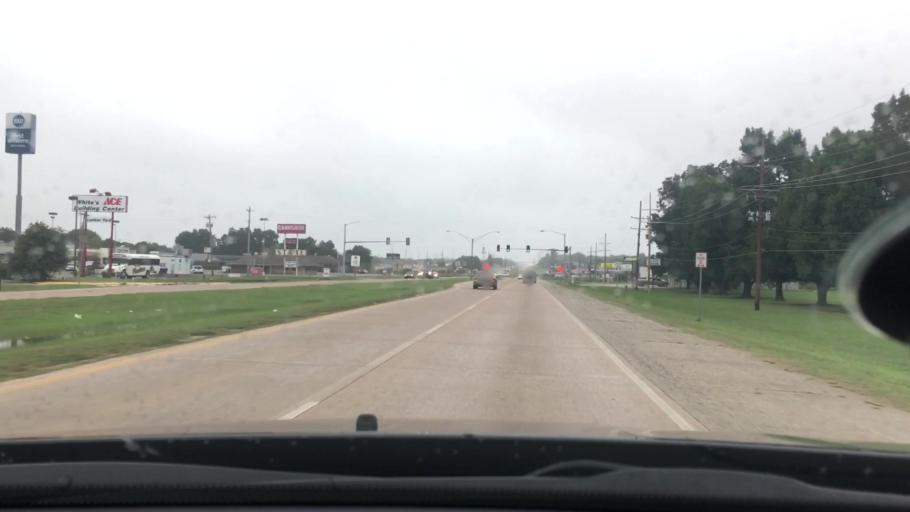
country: US
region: Oklahoma
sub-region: Seminole County
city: Seminole
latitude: 35.2378
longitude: -96.6709
